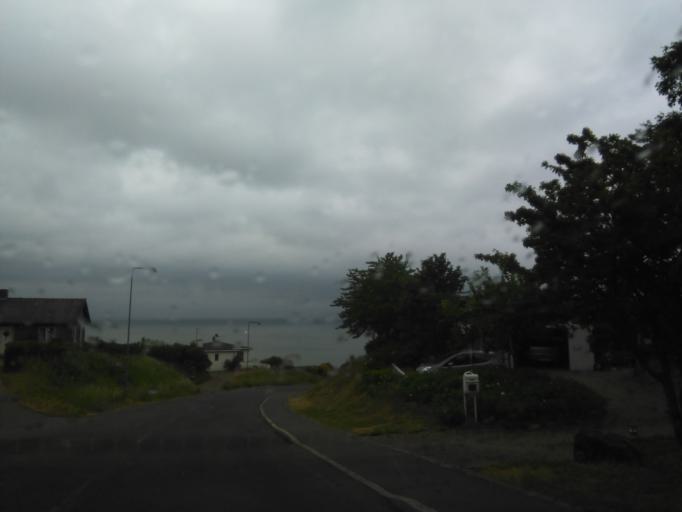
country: DK
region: Capital Region
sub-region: Bornholm Kommune
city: Ronne
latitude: 55.2470
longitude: 14.7387
